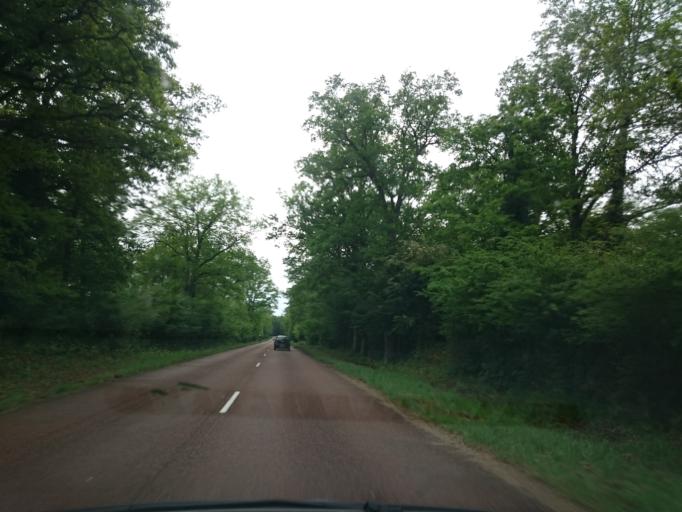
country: FR
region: Centre
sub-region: Departement du Loir-et-Cher
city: Saint-Dye-sur-Loire
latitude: 47.6261
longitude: 1.5115
